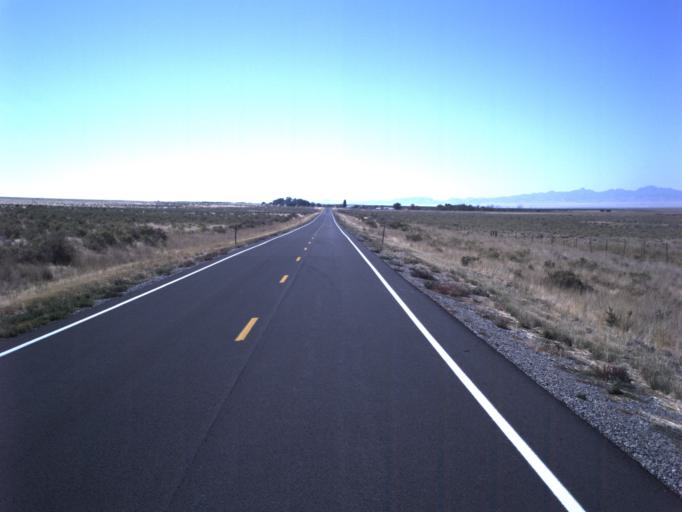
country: US
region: Utah
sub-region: Tooele County
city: Grantsville
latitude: 40.5539
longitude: -112.7388
